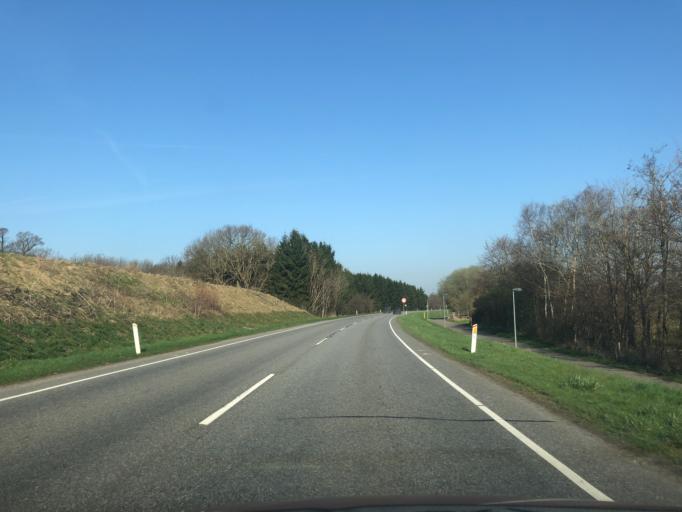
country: DK
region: Zealand
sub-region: Faxe Kommune
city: Haslev
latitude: 55.3164
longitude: 11.9537
